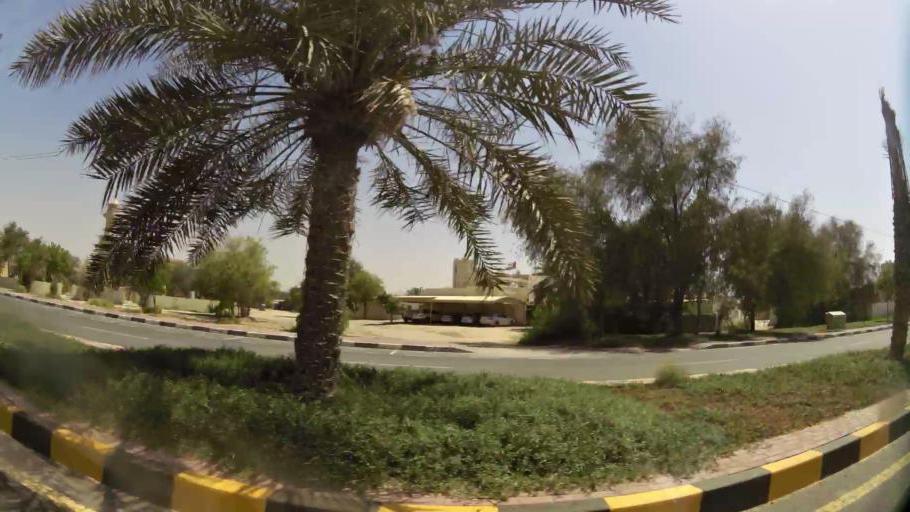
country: AE
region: Ajman
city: Ajman
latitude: 25.4218
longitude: 55.4715
